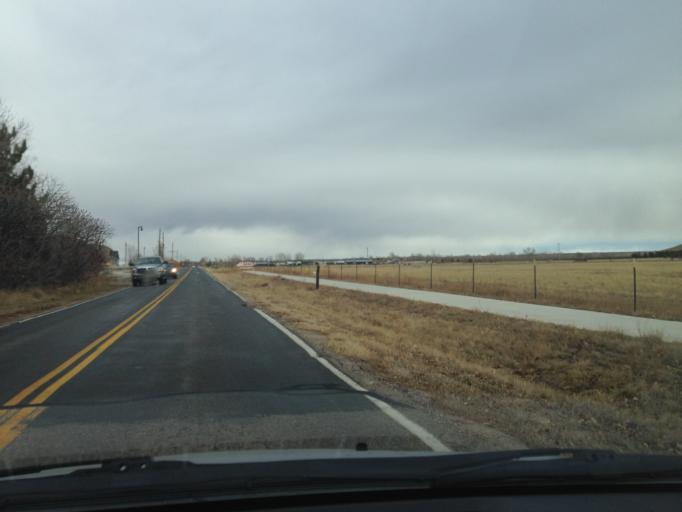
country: US
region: Colorado
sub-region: Weld County
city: Windsor
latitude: 40.5349
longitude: -104.9823
